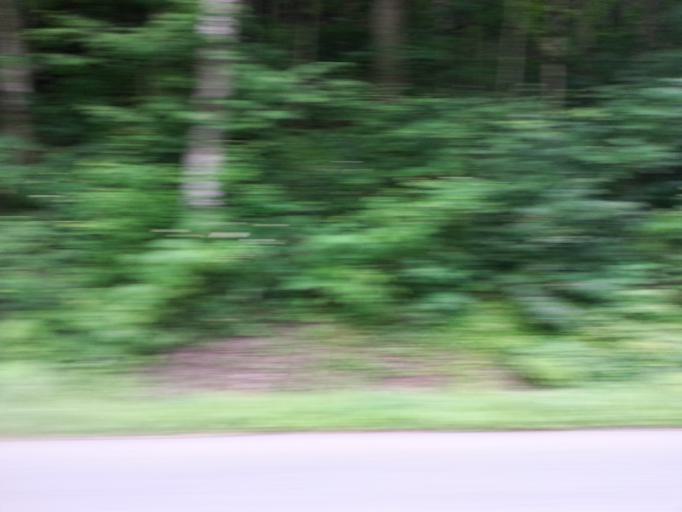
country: US
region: Tennessee
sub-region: Sevier County
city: Pigeon Forge
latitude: 35.6665
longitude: -83.7140
